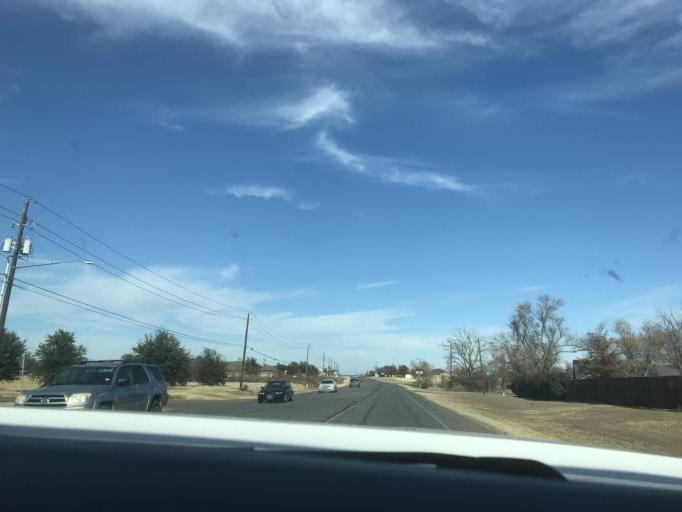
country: US
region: Texas
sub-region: Erath County
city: Stephenville
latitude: 32.2149
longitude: -98.2424
